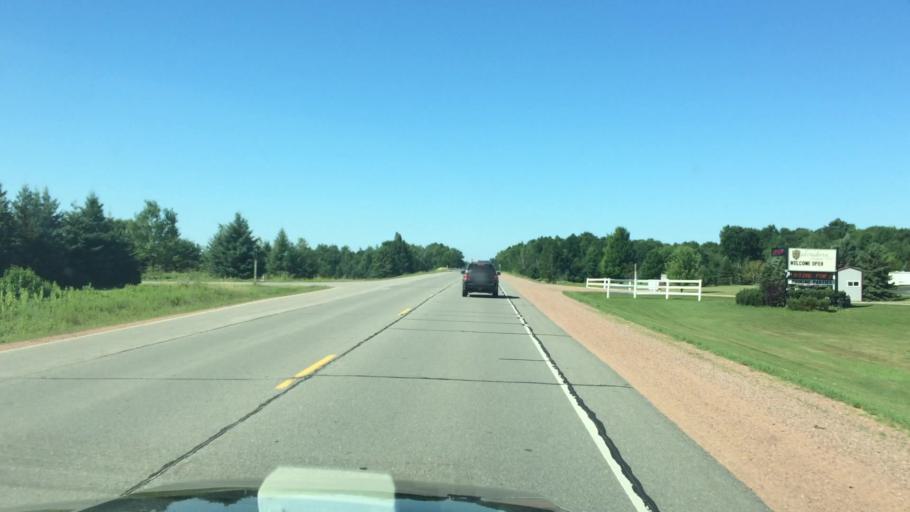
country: US
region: Wisconsin
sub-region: Wood County
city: Marshfield
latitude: 44.7178
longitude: -90.1070
